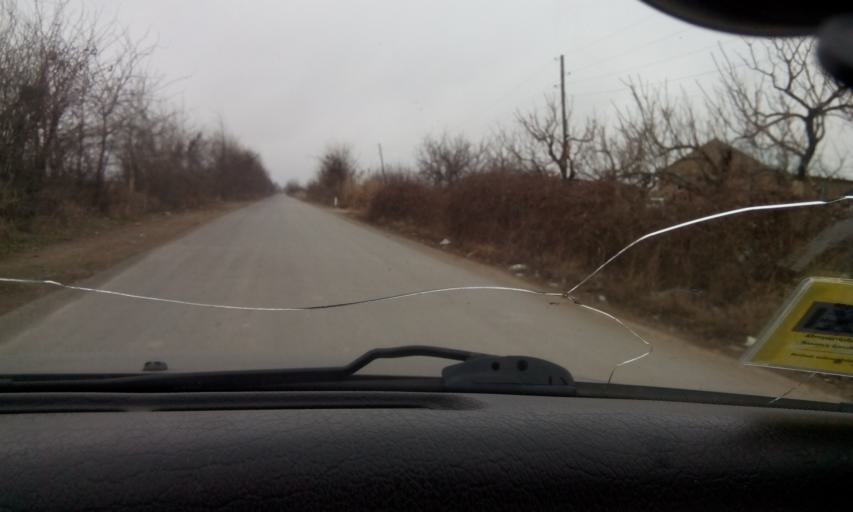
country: AM
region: Armavir
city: Lukashin
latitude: 40.1799
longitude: 43.9818
